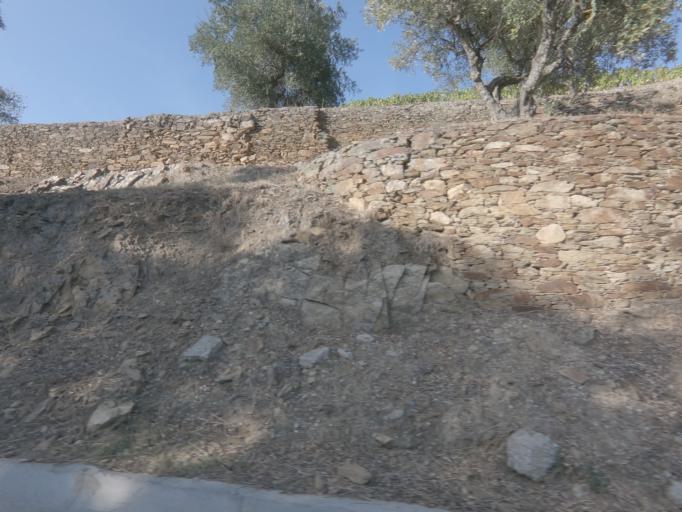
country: PT
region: Vila Real
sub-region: Sabrosa
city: Vilela
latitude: 41.2119
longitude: -7.5417
